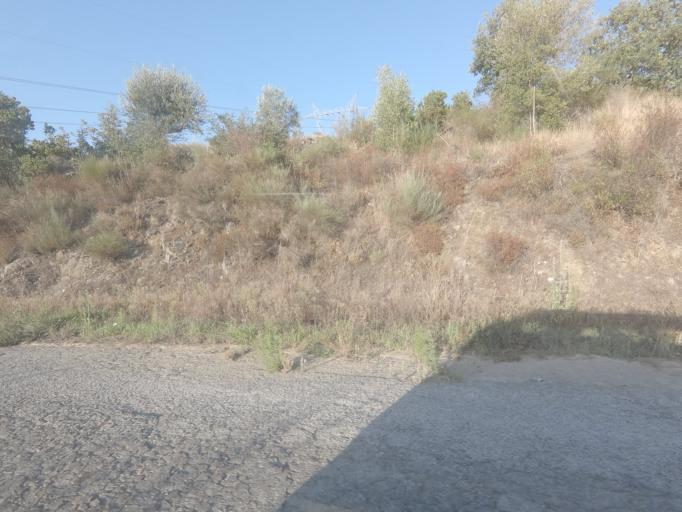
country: PT
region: Viseu
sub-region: Armamar
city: Armamar
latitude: 41.1250
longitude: -7.6722
